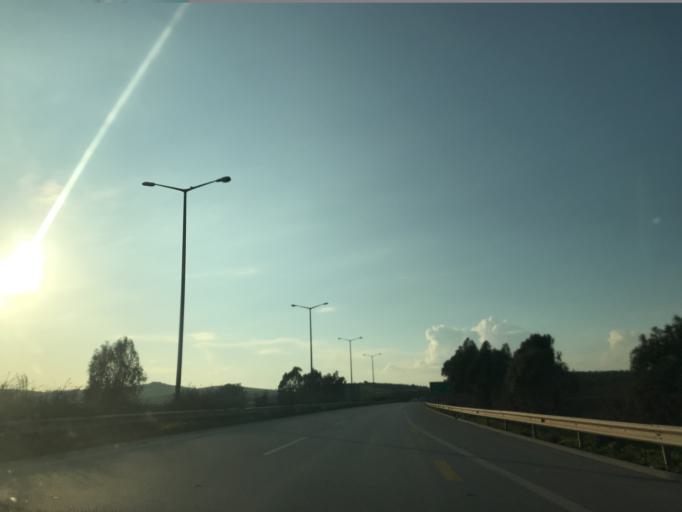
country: TR
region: Osmaniye
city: Toprakkale
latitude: 36.9757
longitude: 36.0096
